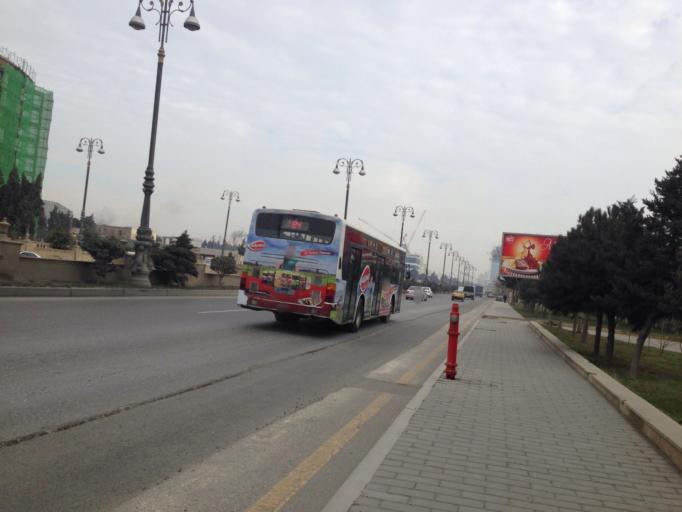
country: AZ
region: Baki
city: Baku
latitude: 40.4056
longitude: 49.8869
